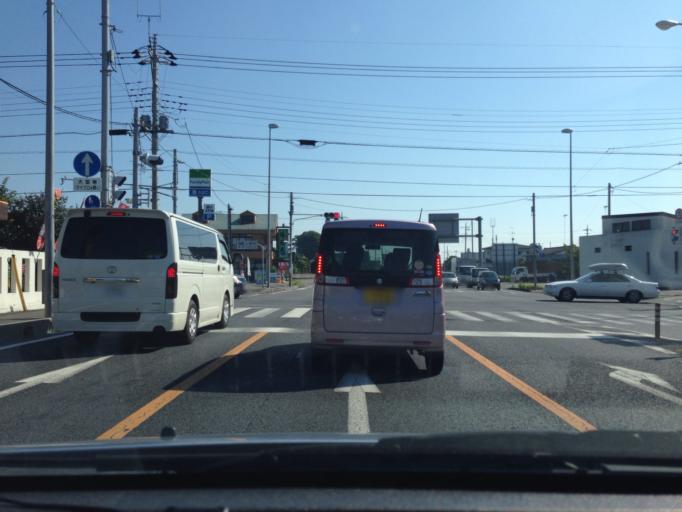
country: JP
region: Ibaraki
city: Naka
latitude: 36.0388
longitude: 140.1754
